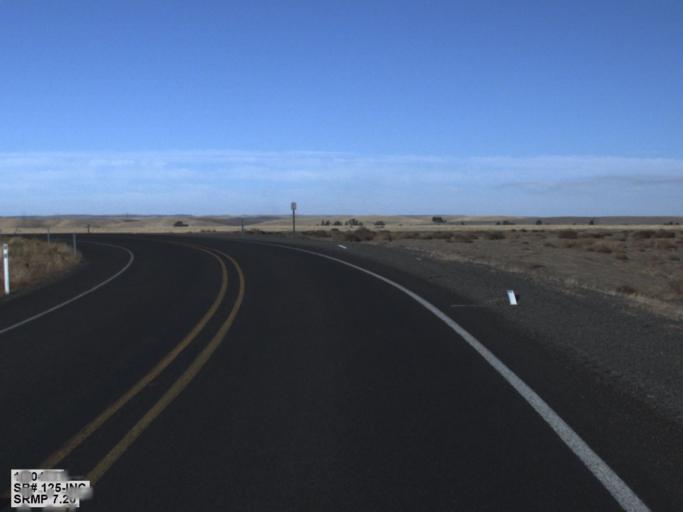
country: US
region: Washington
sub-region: Walla Walla County
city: Walla Walla
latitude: 46.0848
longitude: -118.3567
